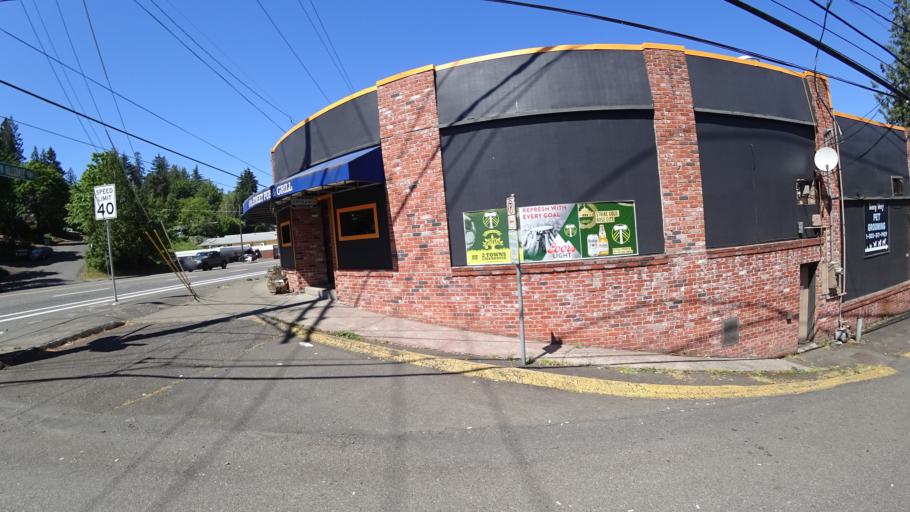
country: US
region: Oregon
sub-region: Washington County
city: Raleigh Hills
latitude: 45.4860
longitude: -122.7233
